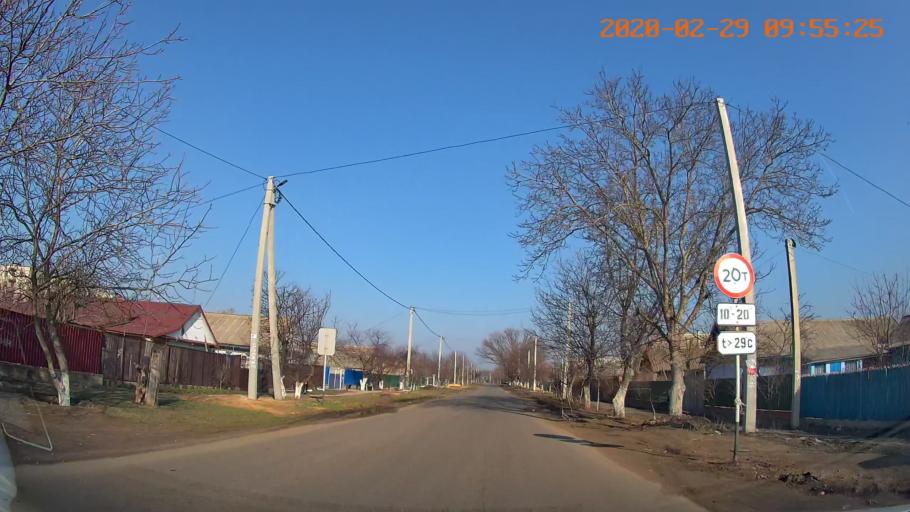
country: MD
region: Telenesti
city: Slobozia
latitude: 46.7337
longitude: 29.7099
